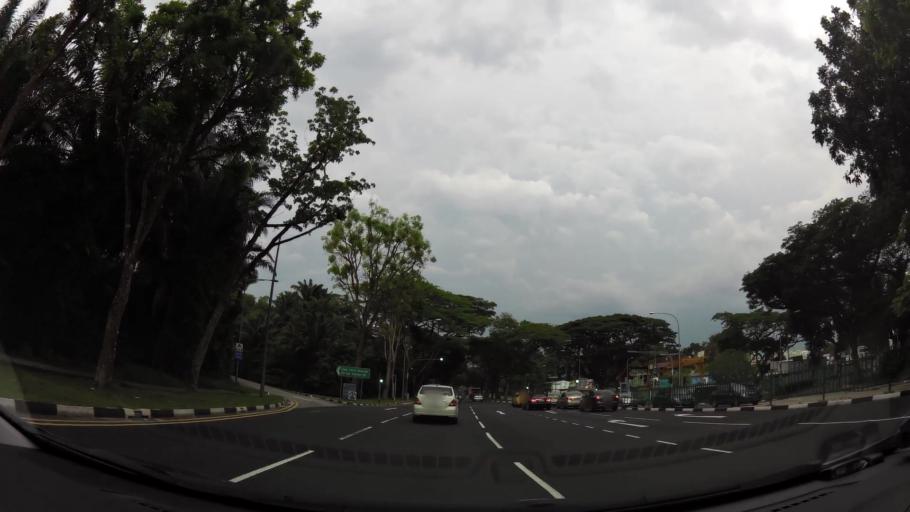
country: SG
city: Singapore
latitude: 1.3675
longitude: 103.8282
